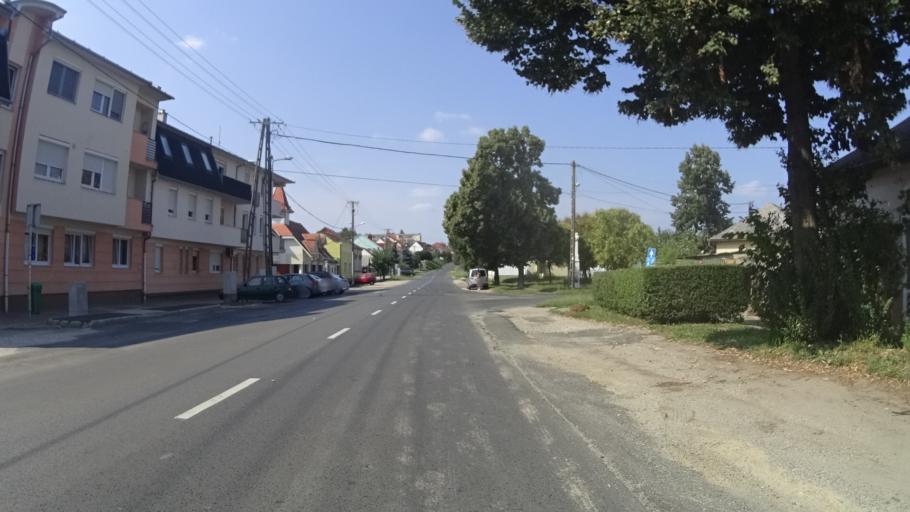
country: HU
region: Zala
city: Nagykanizsa
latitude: 46.4588
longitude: 16.9993
